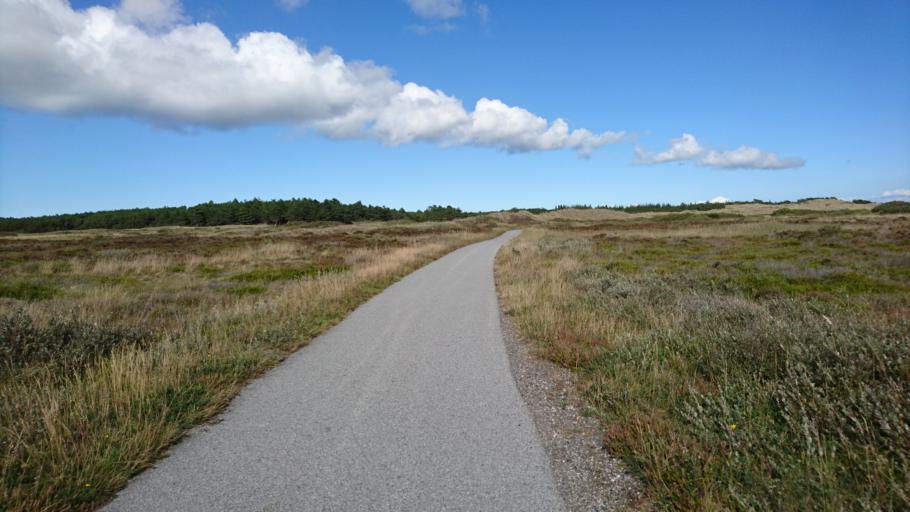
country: DK
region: North Denmark
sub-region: Frederikshavn Kommune
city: Skagen
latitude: 57.6909
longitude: 10.5020
